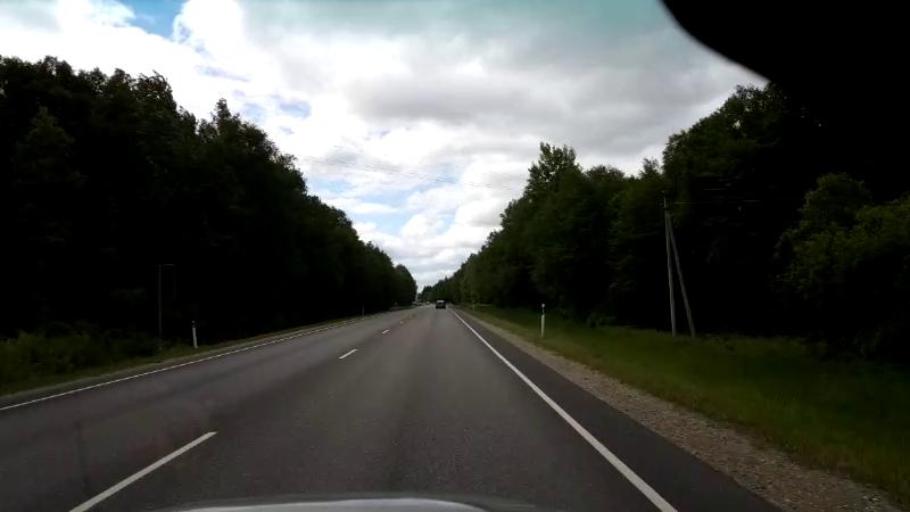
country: EE
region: Paernumaa
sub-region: Halinga vald
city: Parnu-Jaagupi
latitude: 58.6066
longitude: 24.5122
